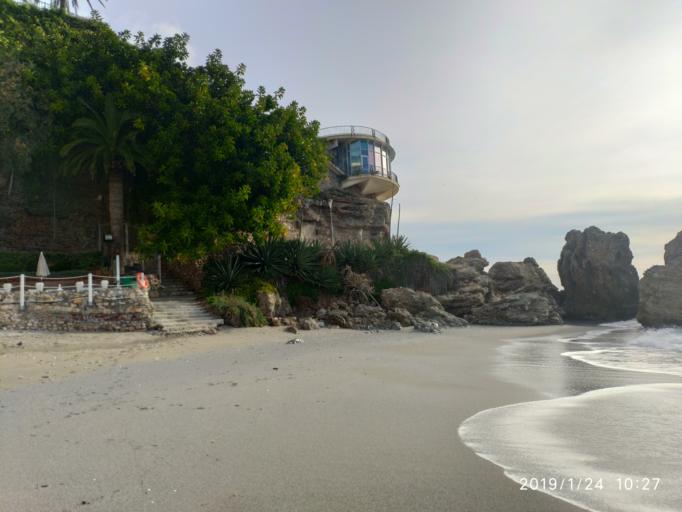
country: ES
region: Andalusia
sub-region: Provincia de Malaga
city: Nerja
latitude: 36.7442
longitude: -3.8761
